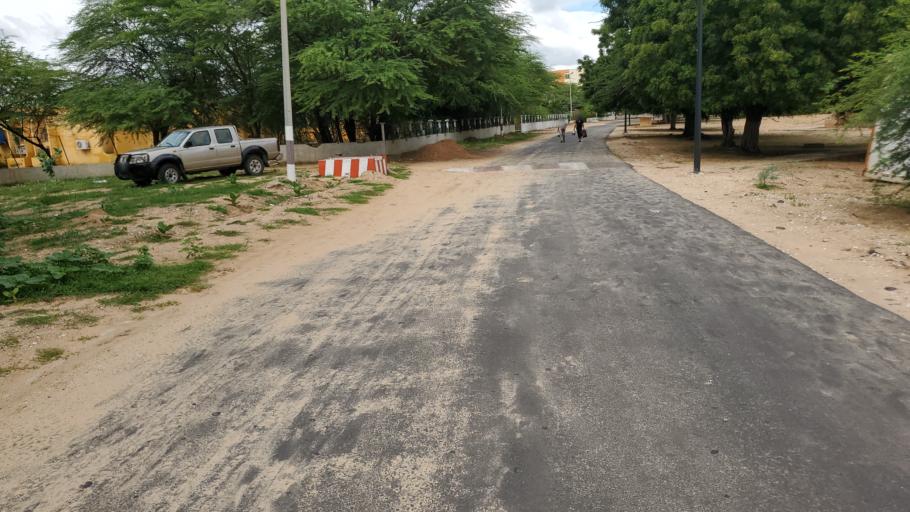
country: SN
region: Saint-Louis
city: Saint-Louis
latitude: 16.0658
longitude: -16.4270
